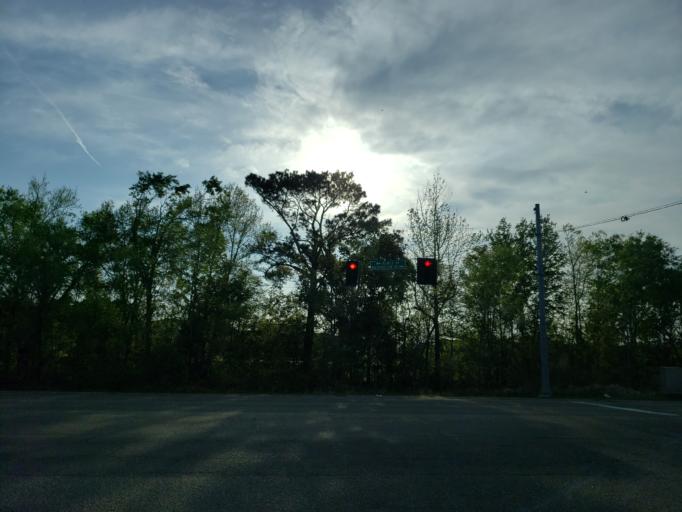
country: US
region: Mississippi
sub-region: Harrison County
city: West Gulfport
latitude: 30.4141
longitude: -89.0576
